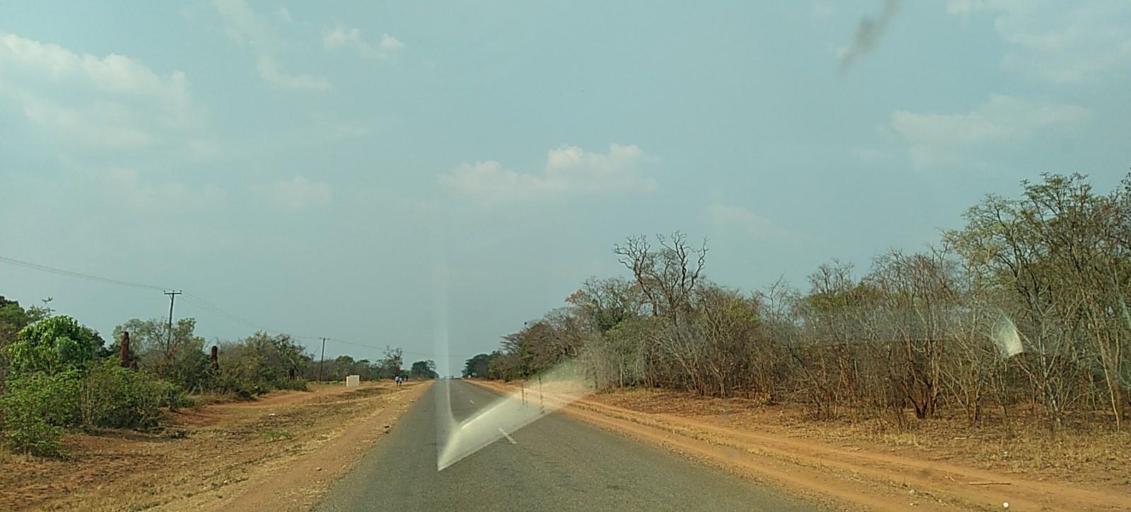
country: ZM
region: North-Western
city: Kabompo
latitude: -13.5814
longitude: 24.2347
